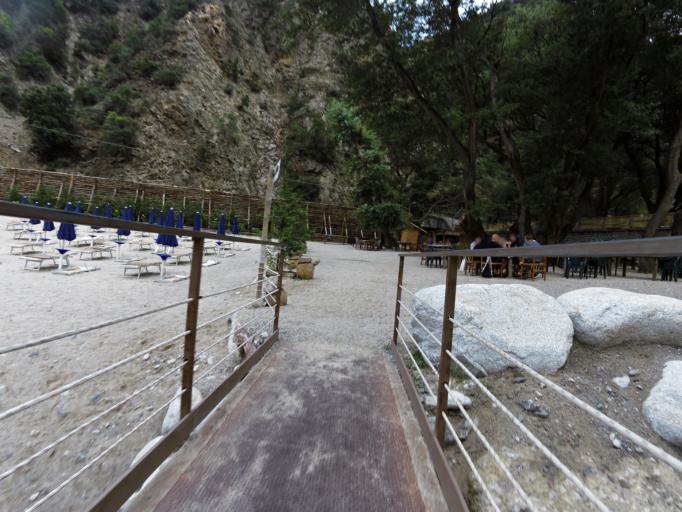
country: IT
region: Calabria
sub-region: Provincia di Reggio Calabria
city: Caulonia
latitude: 38.4246
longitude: 16.3734
